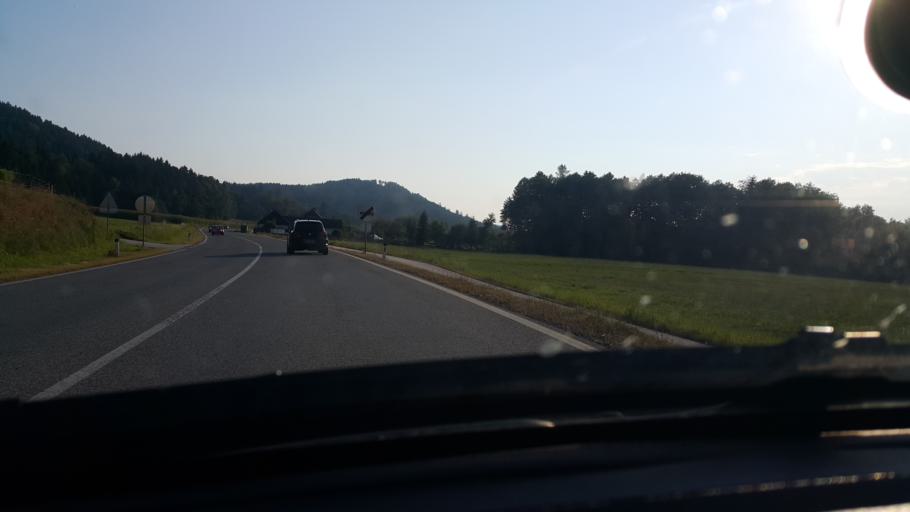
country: AT
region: Carinthia
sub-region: Politischer Bezirk Feldkirchen
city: Glanegg
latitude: 46.6685
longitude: 14.2237
